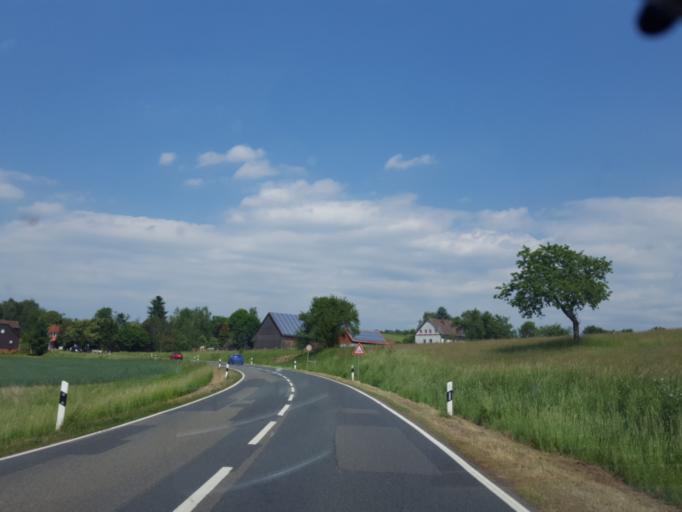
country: DE
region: Lower Saxony
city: Osterode am Harz
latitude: 51.6988
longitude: 10.2492
